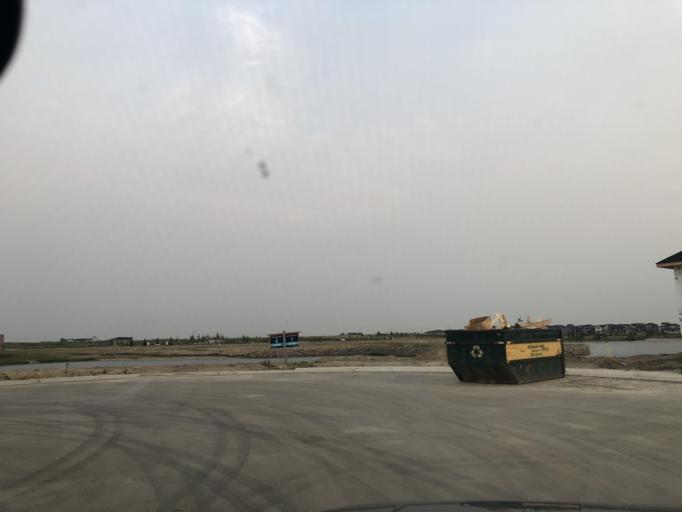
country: CA
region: Alberta
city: Cochrane
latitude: 51.1186
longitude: -114.3925
